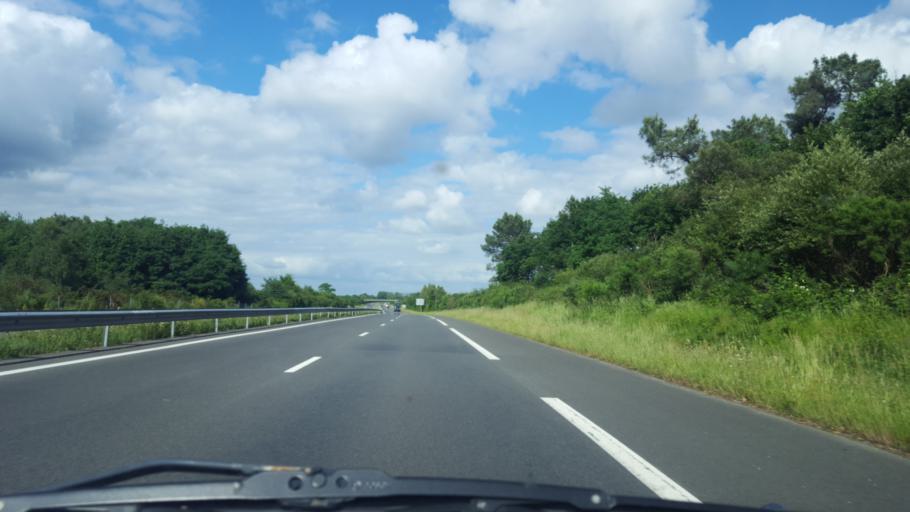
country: FR
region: Pays de la Loire
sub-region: Departement de la Loire-Atlantique
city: Saint-Lumine-de-Coutais
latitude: 47.0124
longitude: -1.7050
